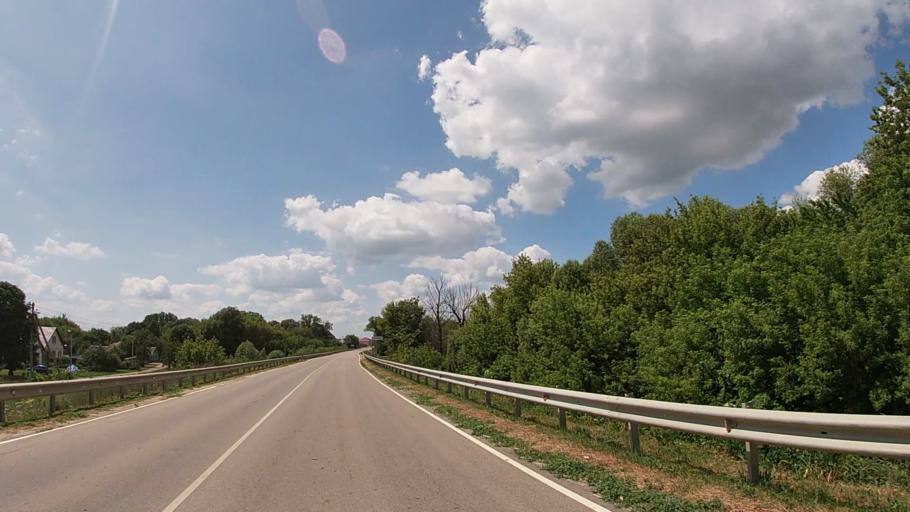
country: RU
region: Belgorod
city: Grayvoron
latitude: 50.4361
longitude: 35.6039
